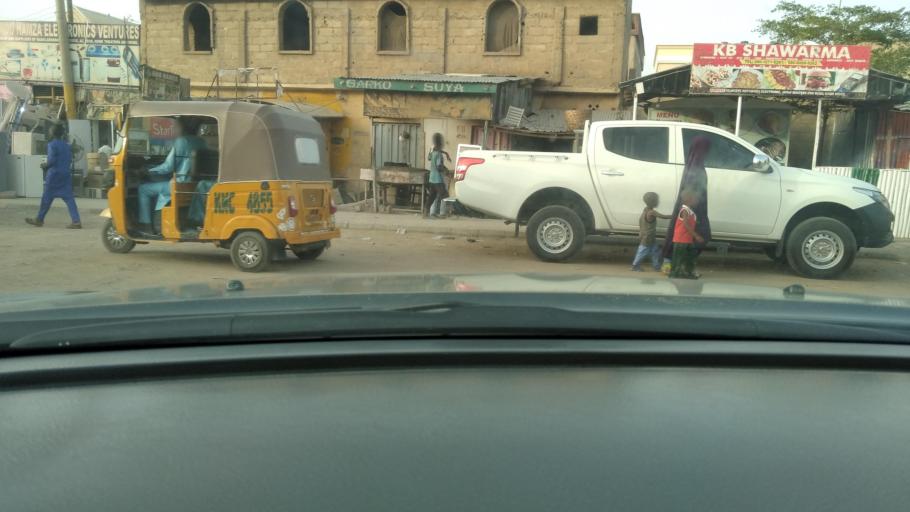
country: NG
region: Kano
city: Kano
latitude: 11.9623
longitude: 8.5266
